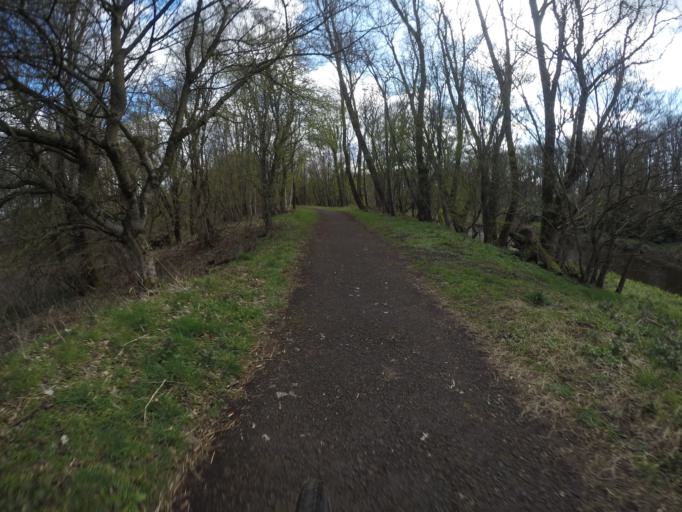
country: GB
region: Scotland
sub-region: North Ayrshire
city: Dreghorn
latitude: 55.5980
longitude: -4.6304
